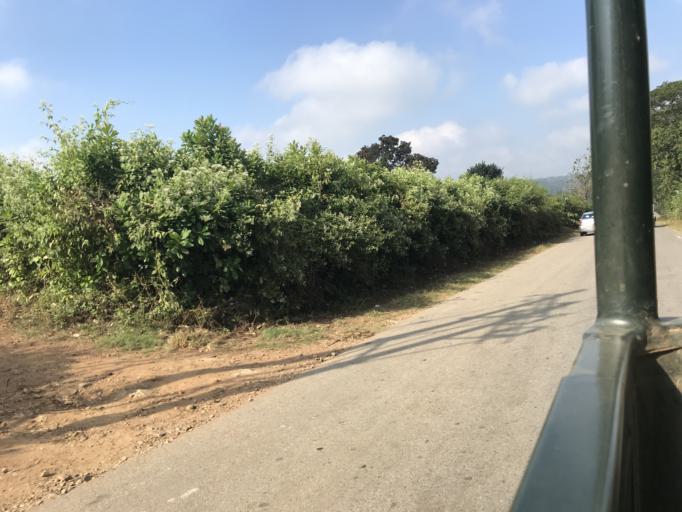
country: IN
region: Karnataka
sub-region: Mysore
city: Heggadadevankote
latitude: 11.9466
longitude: 76.2537
